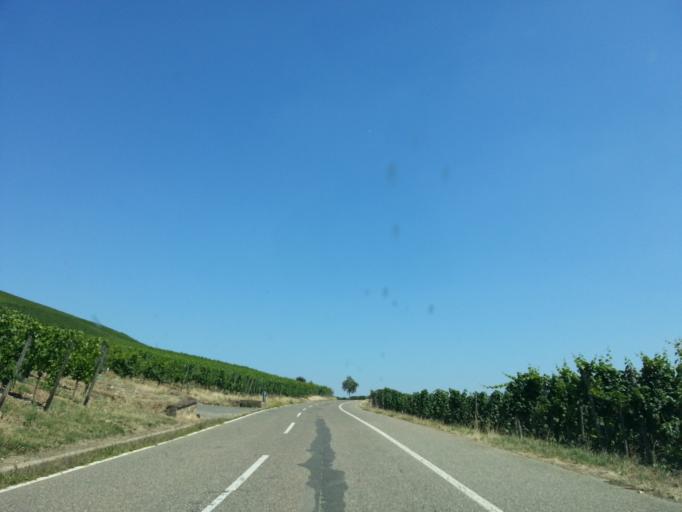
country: DE
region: Rheinland-Pfalz
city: Minheim
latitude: 49.8738
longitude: 6.9413
